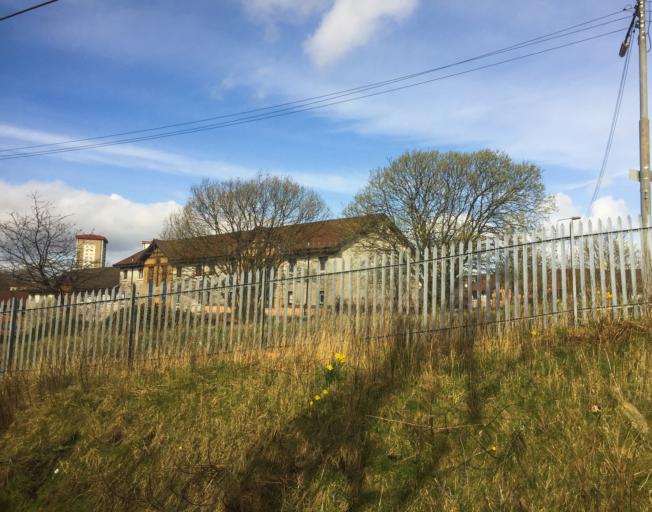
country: GB
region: Scotland
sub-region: East Dunbartonshire
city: Bishopbriggs
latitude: 55.8838
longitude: -4.2357
